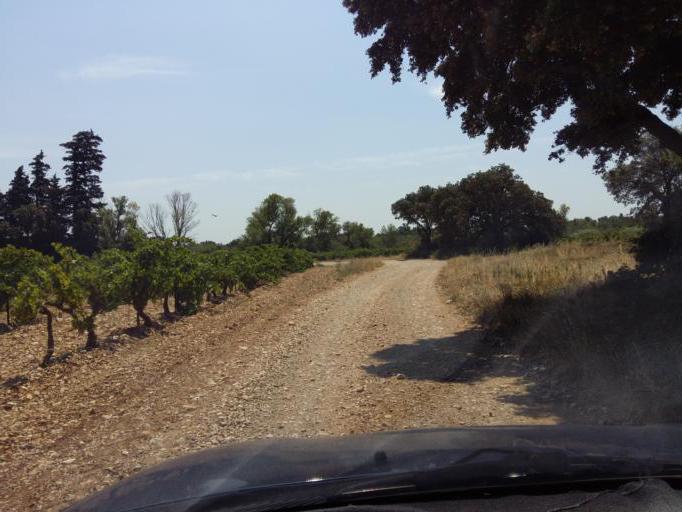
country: FR
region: Provence-Alpes-Cote d'Azur
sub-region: Departement du Vaucluse
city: Camaret-sur-Aigues
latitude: 44.1790
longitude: 4.8736
